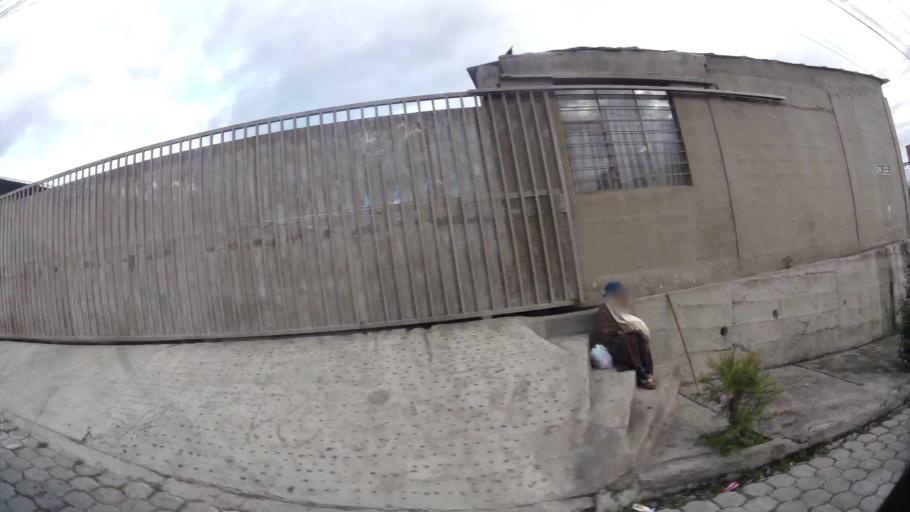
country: EC
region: Pichincha
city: Quito
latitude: -0.1491
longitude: -78.4634
